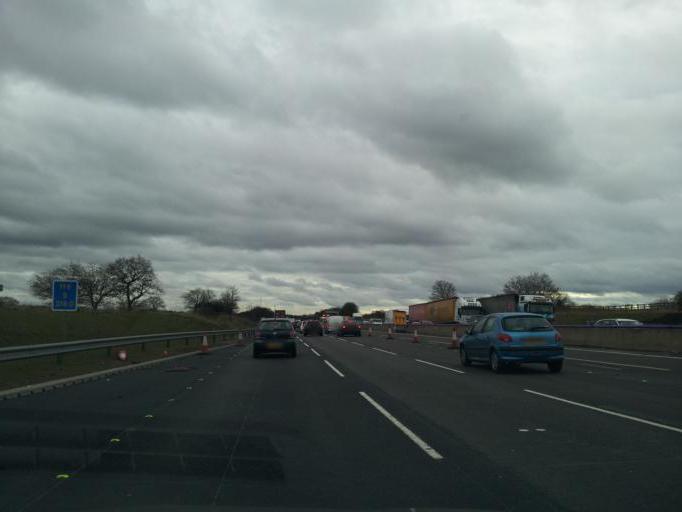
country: GB
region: England
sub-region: Staffordshire
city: Penkridge
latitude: 52.7478
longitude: -2.1000
